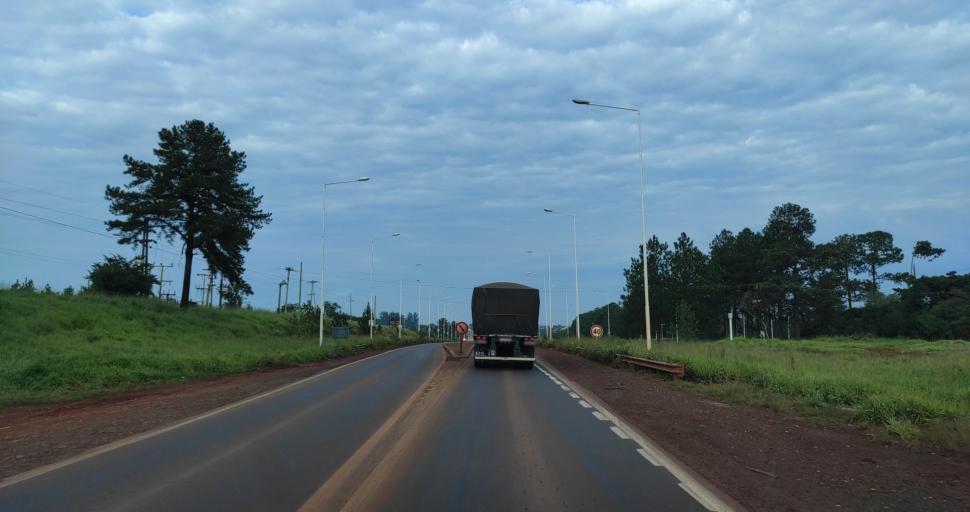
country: AR
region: Corrientes
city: Gobernador Ingeniero Valentin Virasoro
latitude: -27.9659
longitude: -56.0073
